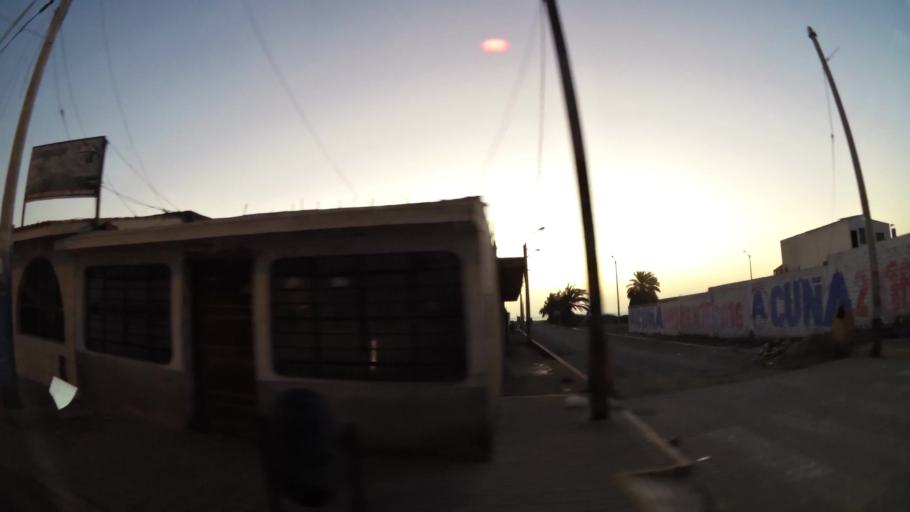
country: PE
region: Ica
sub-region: Provincia de Pisco
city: Pisco
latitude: -13.7134
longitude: -76.2189
